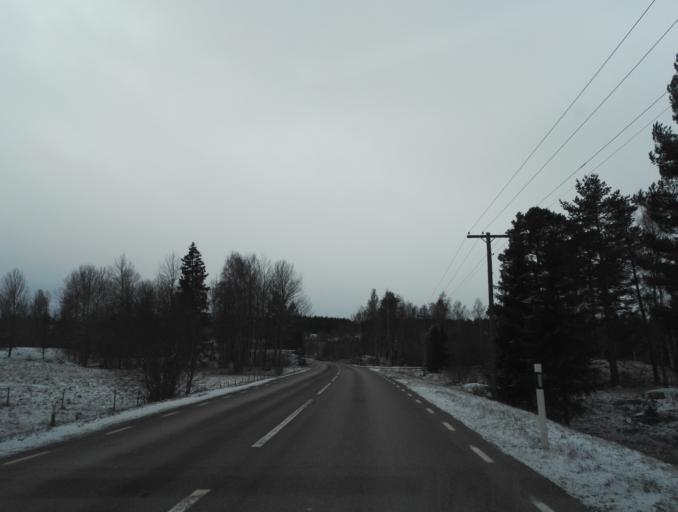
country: SE
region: Kalmar
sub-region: Hultsfreds Kommun
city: Virserum
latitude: 57.2909
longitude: 15.5655
